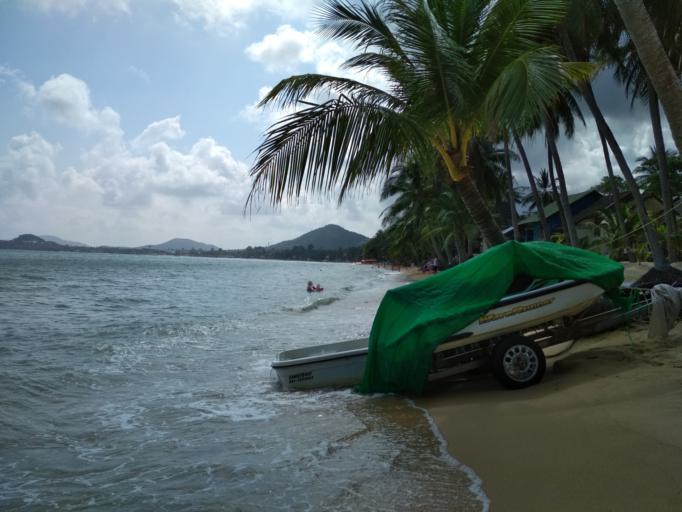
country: TH
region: Surat Thani
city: Ko Samui
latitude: 9.5758
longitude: 99.9914
